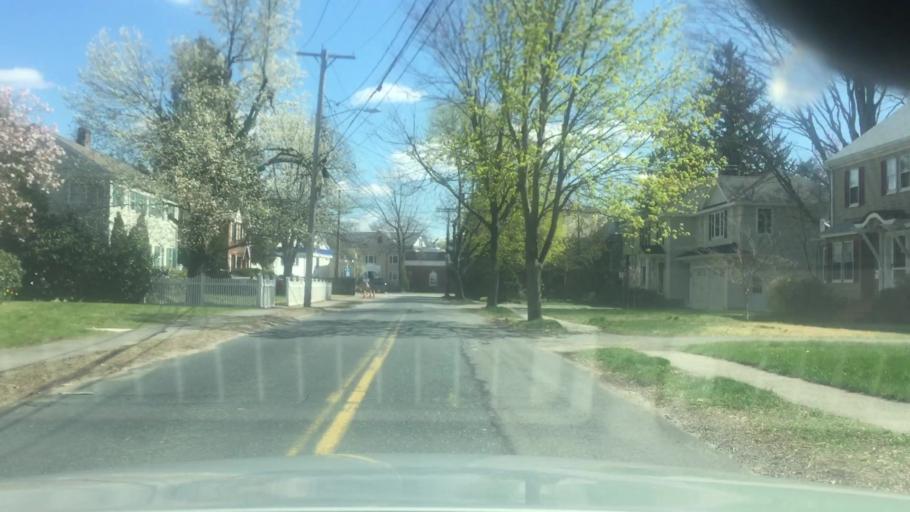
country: US
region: Massachusetts
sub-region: Norfolk County
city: Needham
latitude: 42.2813
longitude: -71.2403
